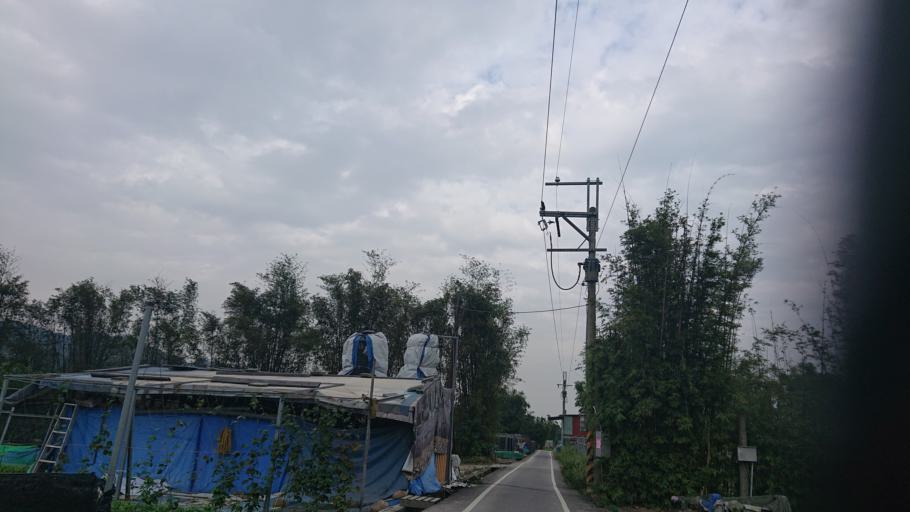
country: TW
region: Taiwan
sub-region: Taoyuan
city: Taoyuan
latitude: 24.9501
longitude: 121.3659
